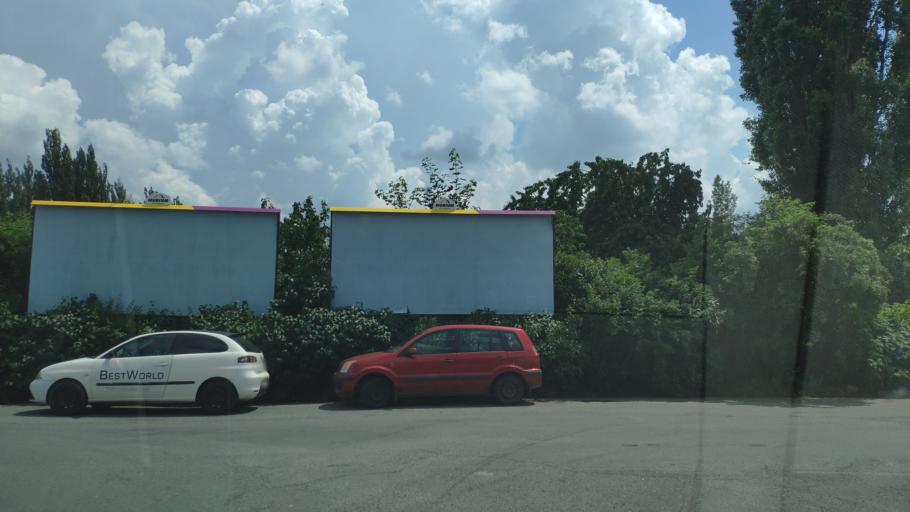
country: SK
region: Kosicky
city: Kosice
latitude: 48.6792
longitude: 21.2937
